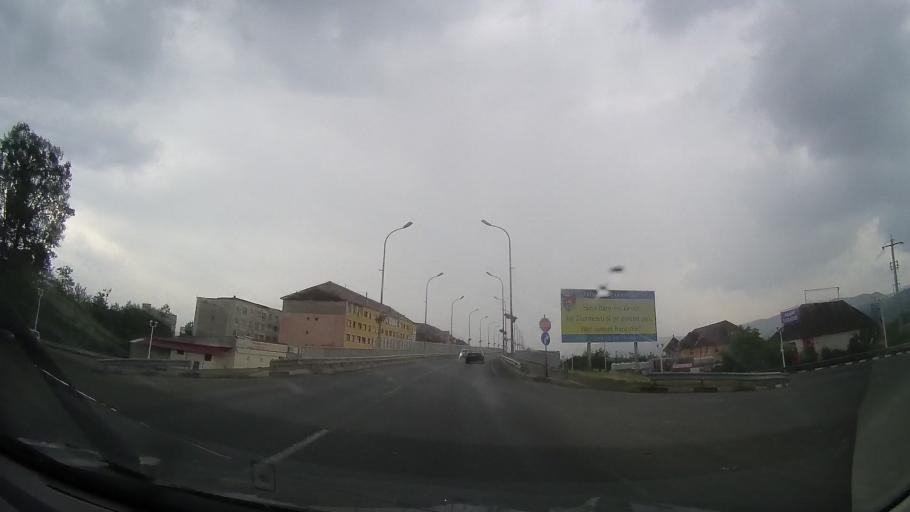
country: RO
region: Caras-Severin
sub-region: Comuna Buchin
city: Buchin
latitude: 45.3873
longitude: 22.2295
